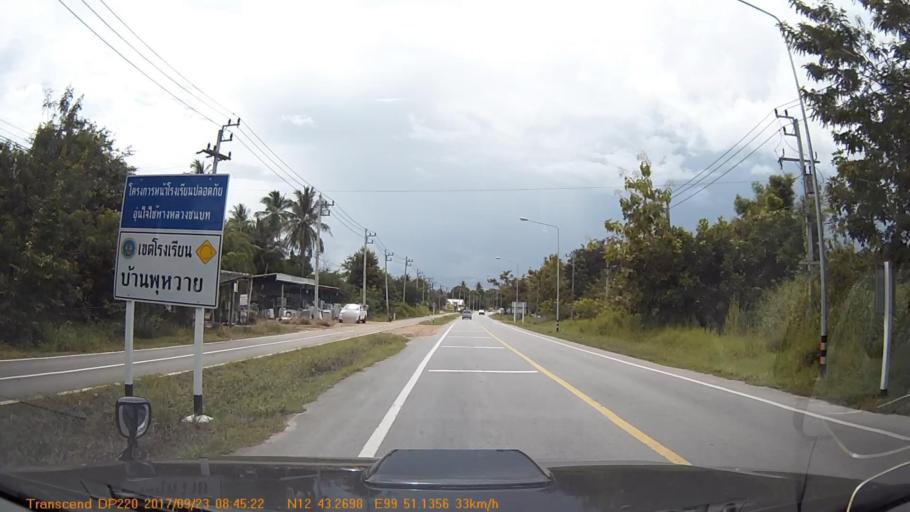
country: TH
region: Phetchaburi
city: Cha-am
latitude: 12.7210
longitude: 99.8523
